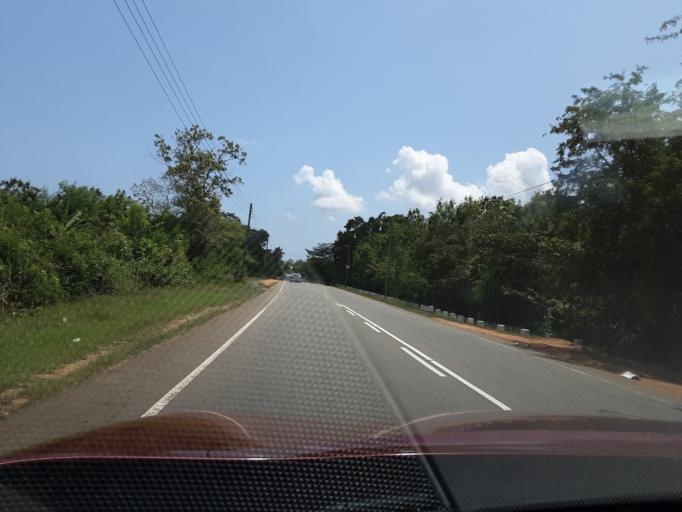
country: LK
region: Southern
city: Tangalla
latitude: 6.2142
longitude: 81.2066
